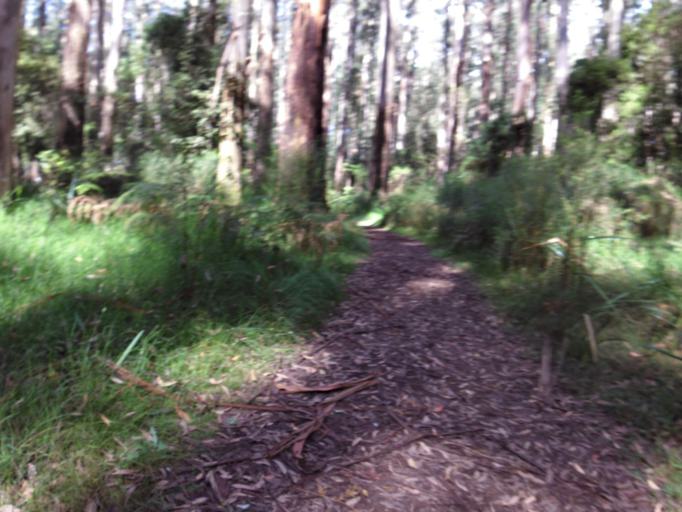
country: AU
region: Victoria
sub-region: Yarra Ranges
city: Ferny Creek
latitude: -37.8837
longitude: 145.3491
